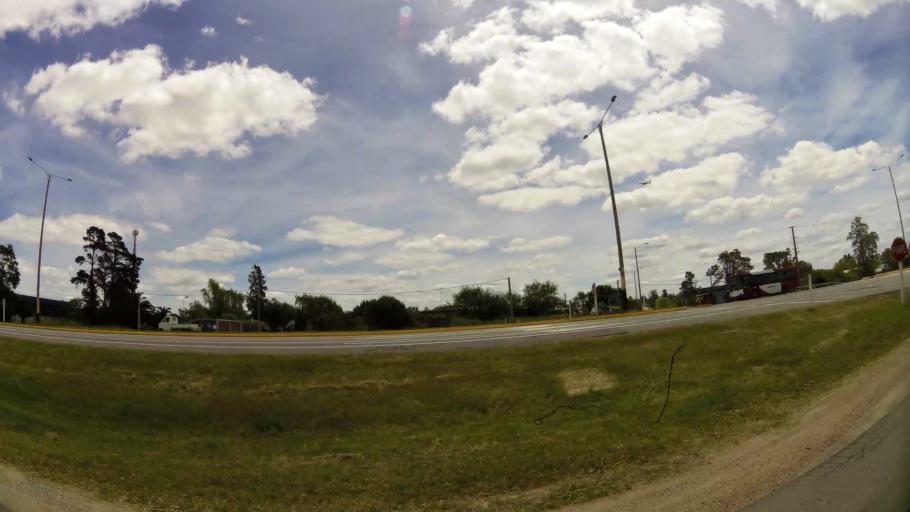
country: UY
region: Canelones
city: Colonia Nicolich
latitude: -34.8062
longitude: -55.9583
